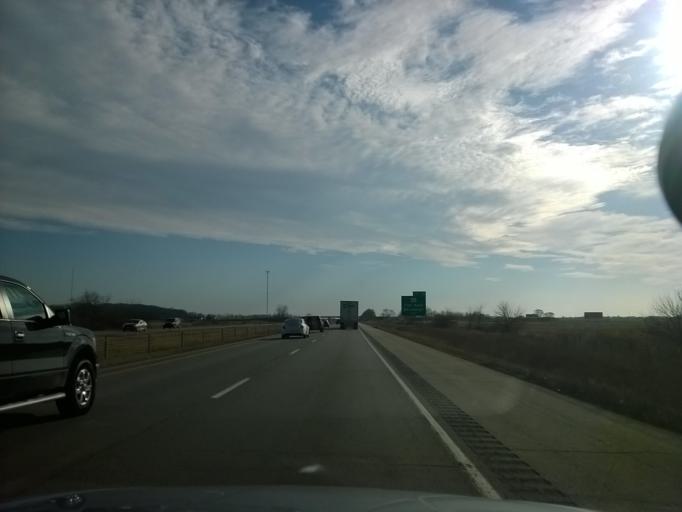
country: US
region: Indiana
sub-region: Johnson County
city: Edinburgh
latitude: 39.3842
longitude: -85.9430
